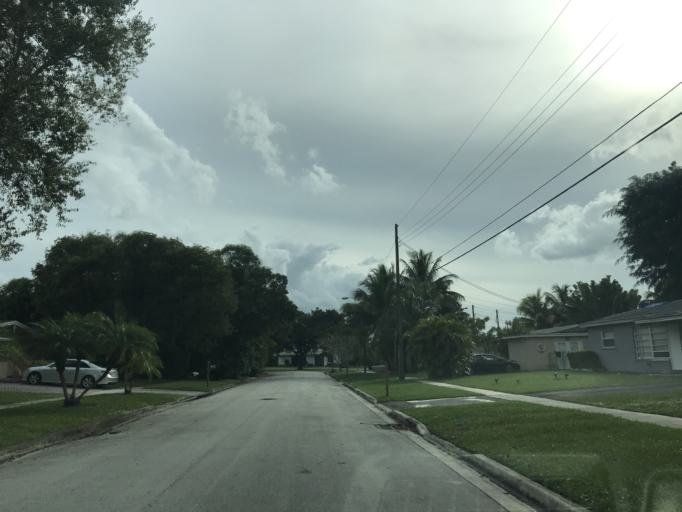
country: US
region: Florida
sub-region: Broward County
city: Margate
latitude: 26.2562
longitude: -80.2081
